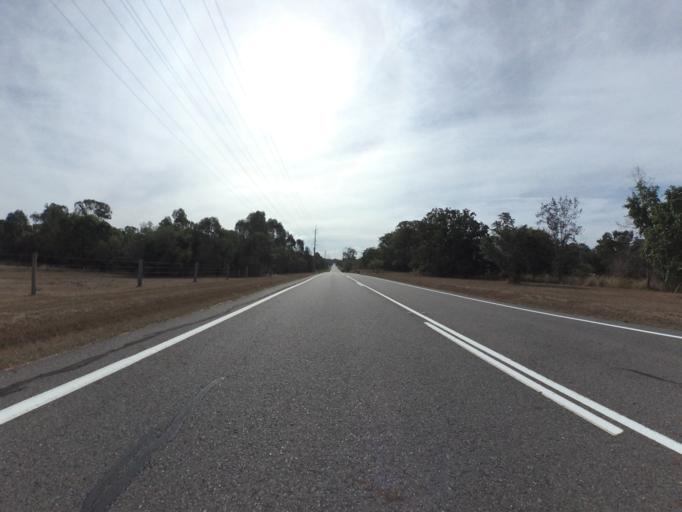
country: AU
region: Queensland
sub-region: Brisbane
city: Moggill
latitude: -27.5891
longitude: 152.8607
